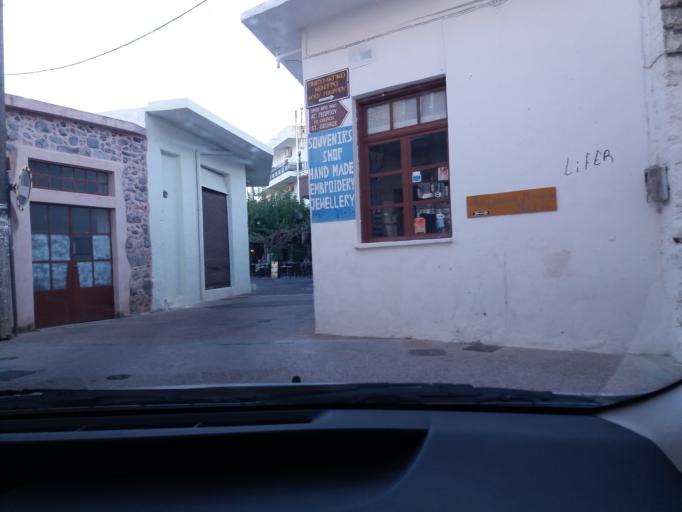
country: GR
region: Crete
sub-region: Nomos Irakleiou
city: Mokhos
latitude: 35.2641
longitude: 25.4228
